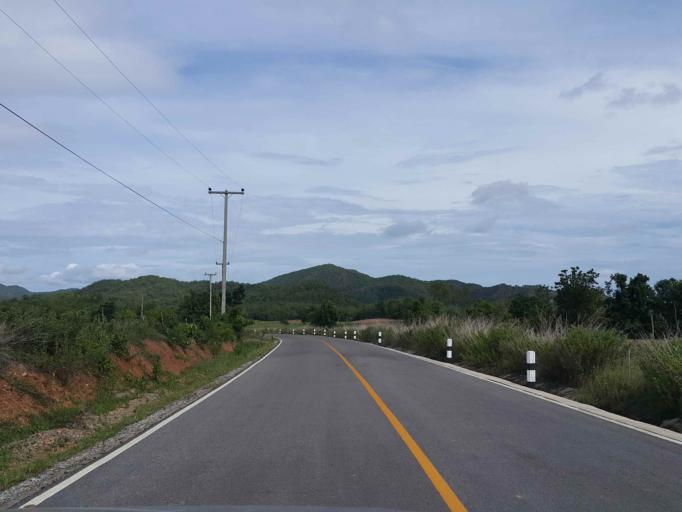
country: TH
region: Sukhothai
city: Thung Saliam
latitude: 17.2359
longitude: 99.5072
